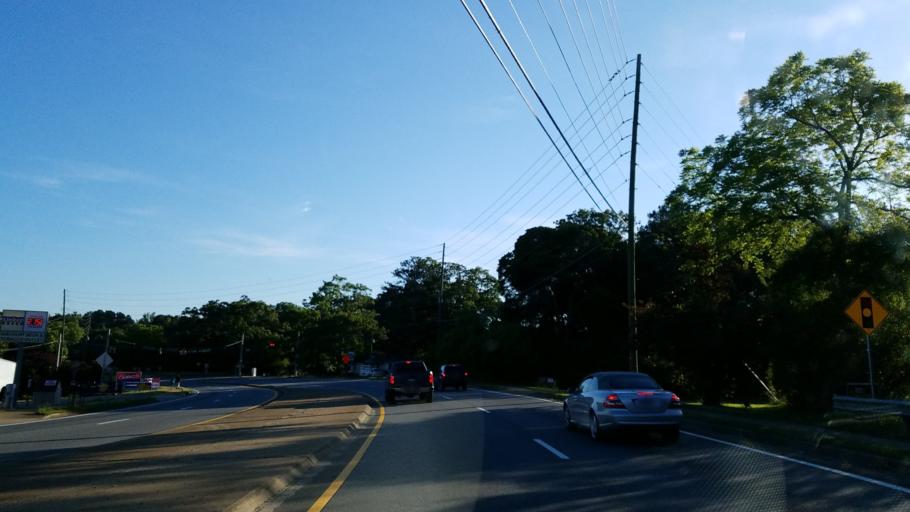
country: US
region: Georgia
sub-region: Cherokee County
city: Woodstock
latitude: 34.0973
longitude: -84.5821
